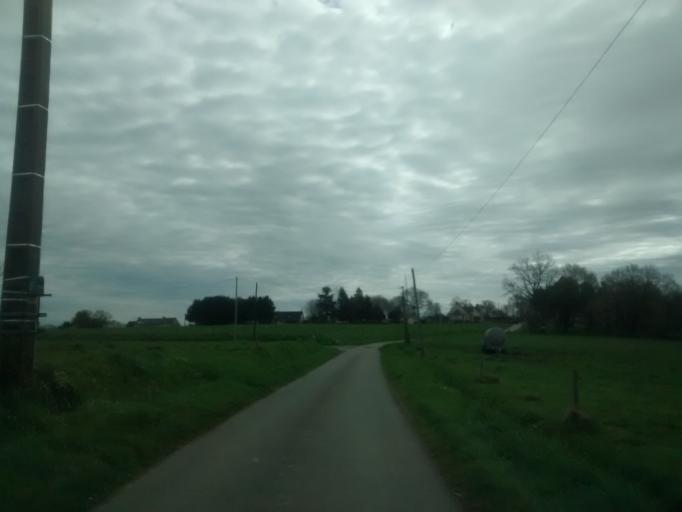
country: FR
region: Brittany
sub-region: Departement d'Ille-et-Vilaine
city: Chasne-sur-Illet
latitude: 48.2481
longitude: -1.5469
